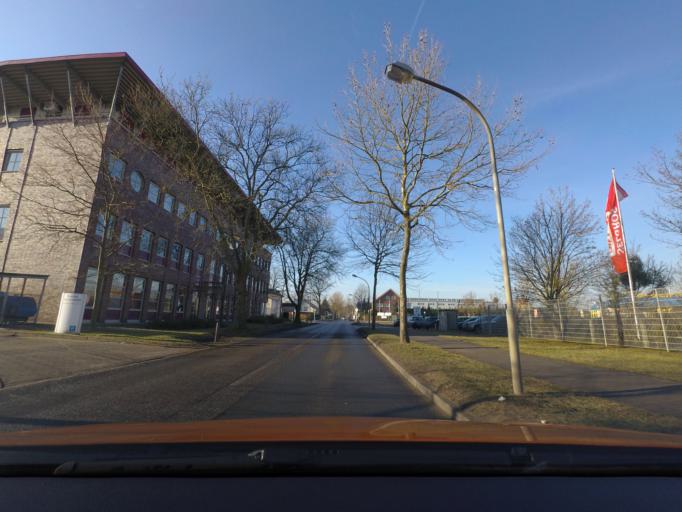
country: DE
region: Brandenburg
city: Falkensee
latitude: 52.5535
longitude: 13.1019
